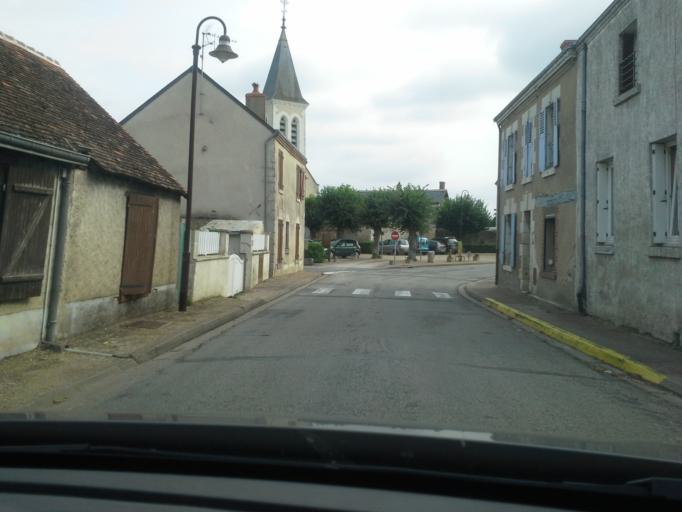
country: FR
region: Centre
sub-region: Departement du Loir-et-Cher
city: Herbault
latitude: 47.5899
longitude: 1.1993
